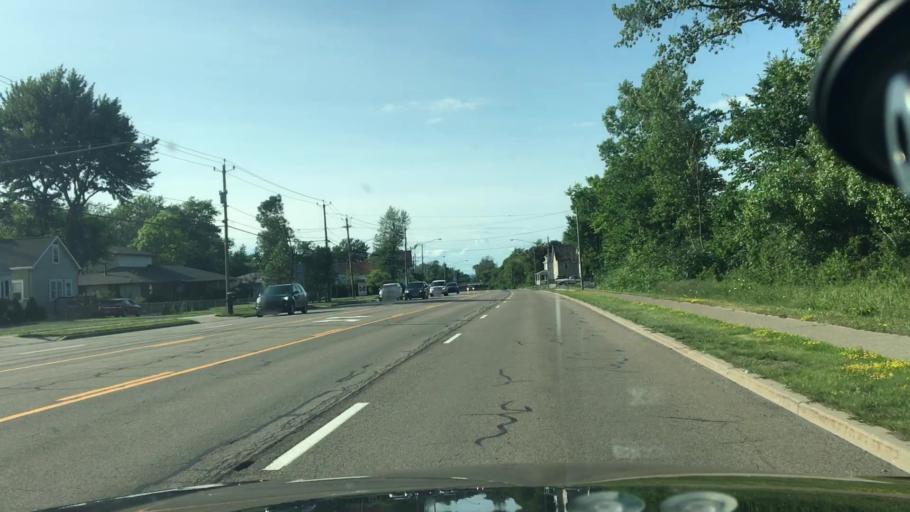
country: US
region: New York
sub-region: Erie County
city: Wanakah
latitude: 42.7609
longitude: -78.8621
